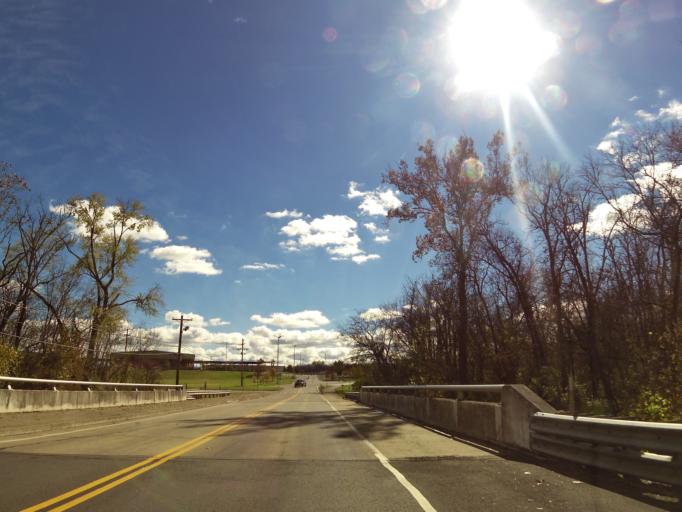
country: US
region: Tennessee
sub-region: Blount County
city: Alcoa
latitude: 35.7926
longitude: -83.9709
